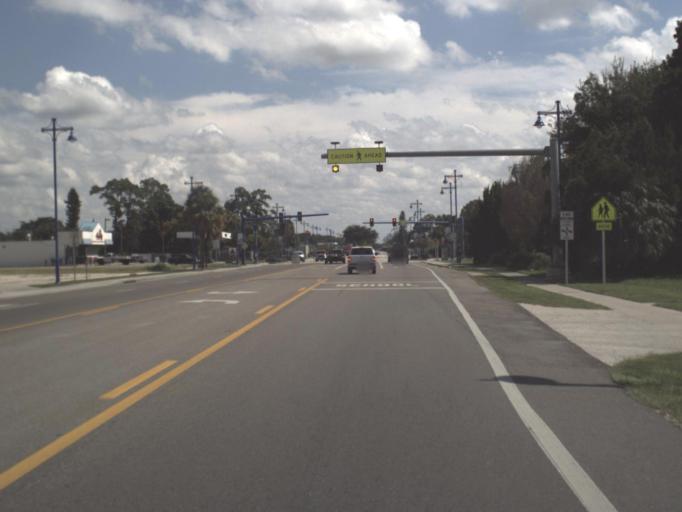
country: US
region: Florida
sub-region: Collier County
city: Immokalee
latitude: 26.4184
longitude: -81.4270
